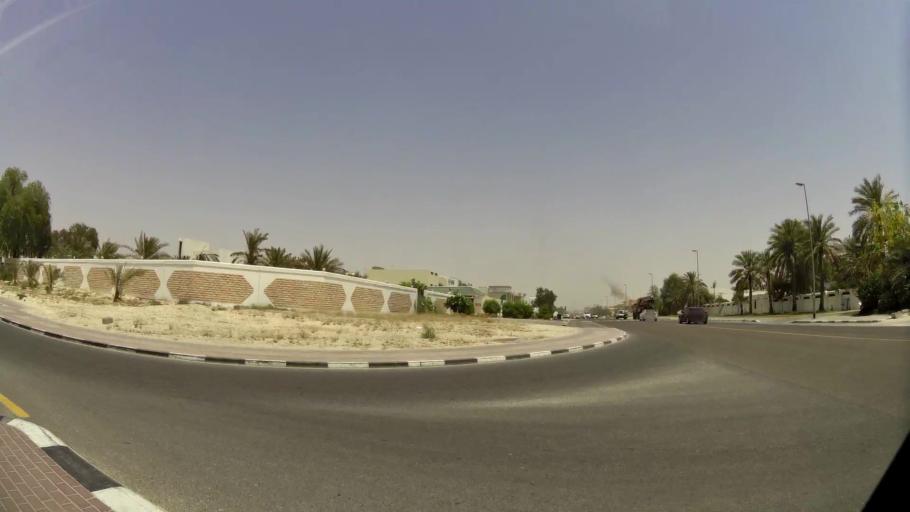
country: AE
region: Dubai
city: Dubai
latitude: 25.1218
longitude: 55.1783
